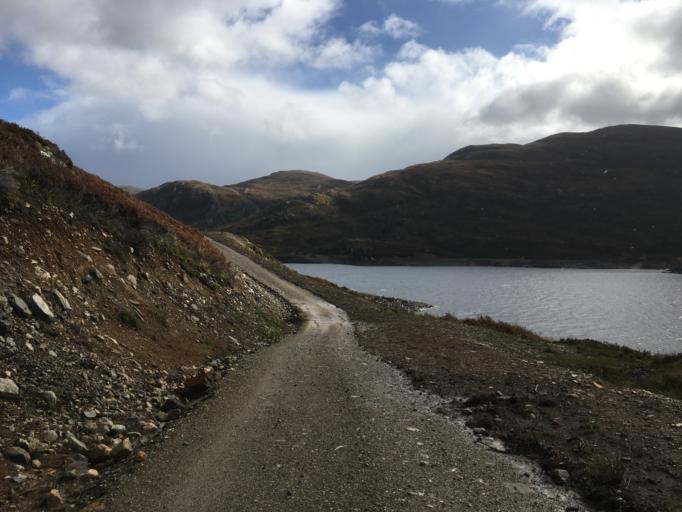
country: GB
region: Scotland
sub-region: Highland
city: Spean Bridge
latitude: 57.3402
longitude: -4.9690
